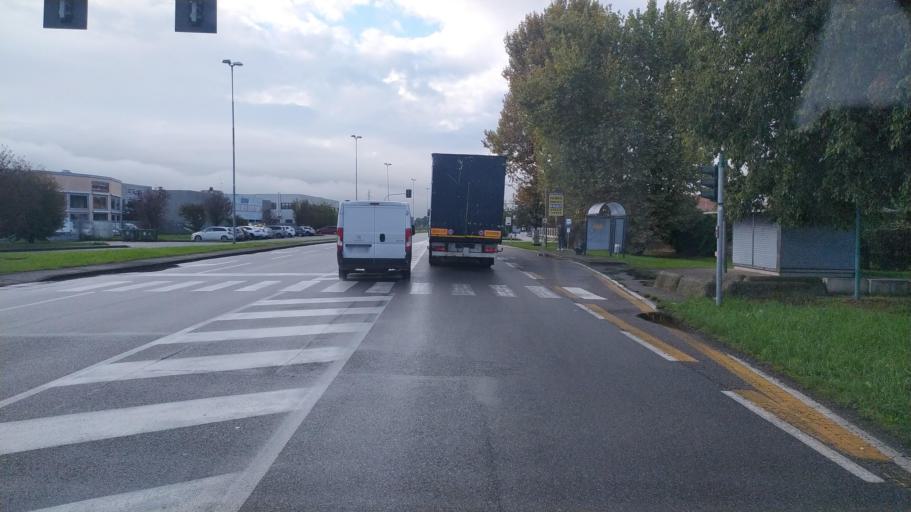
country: IT
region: Lombardy
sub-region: Citta metropolitana di Milano
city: Gaggiano
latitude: 45.3804
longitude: 9.0282
